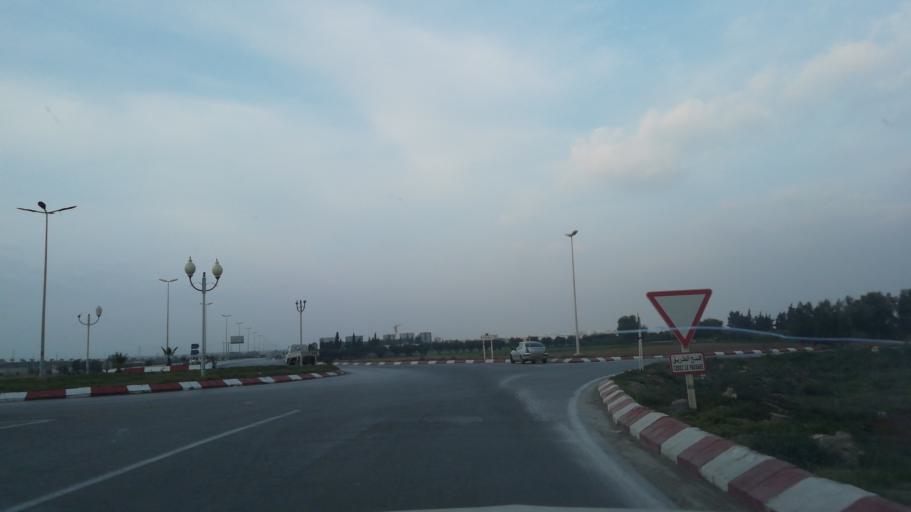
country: DZ
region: Sidi Bel Abbes
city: Sidi Bel Abbes
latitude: 35.1949
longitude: -0.6615
